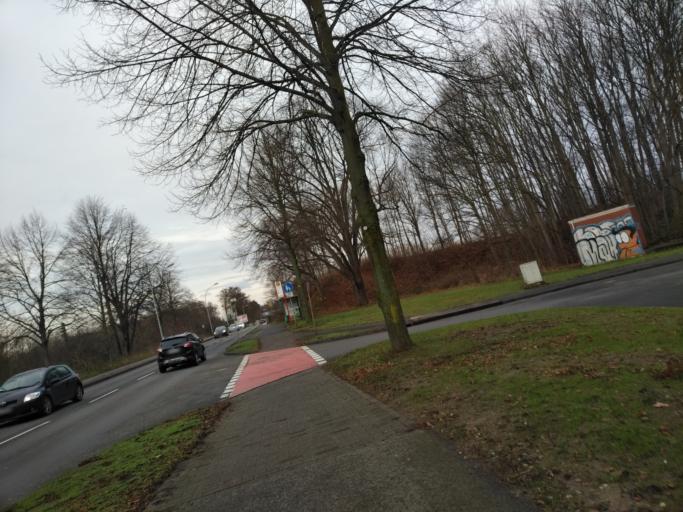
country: DE
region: North Rhine-Westphalia
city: Opladen
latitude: 51.0454
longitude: 7.0208
